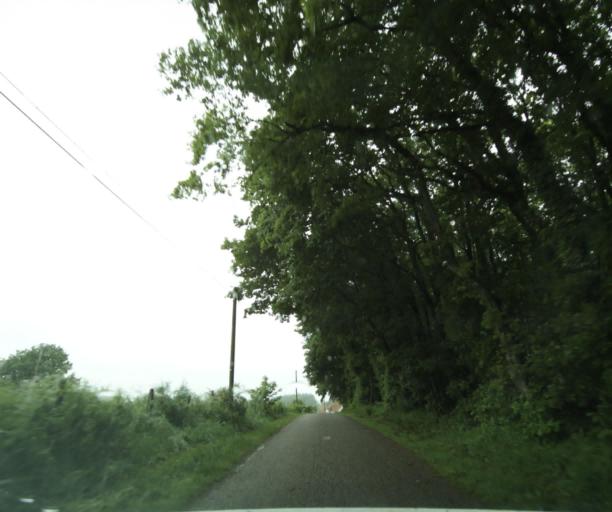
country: FR
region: Bourgogne
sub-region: Departement de Saone-et-Loire
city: Charolles
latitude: 46.4212
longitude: 4.3740
